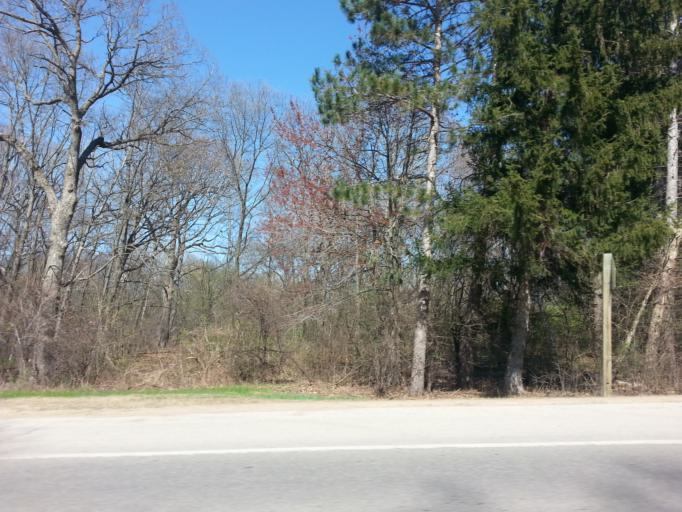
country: US
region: Wisconsin
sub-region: Dunn County
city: Menomonie
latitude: 44.8563
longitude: -91.9271
